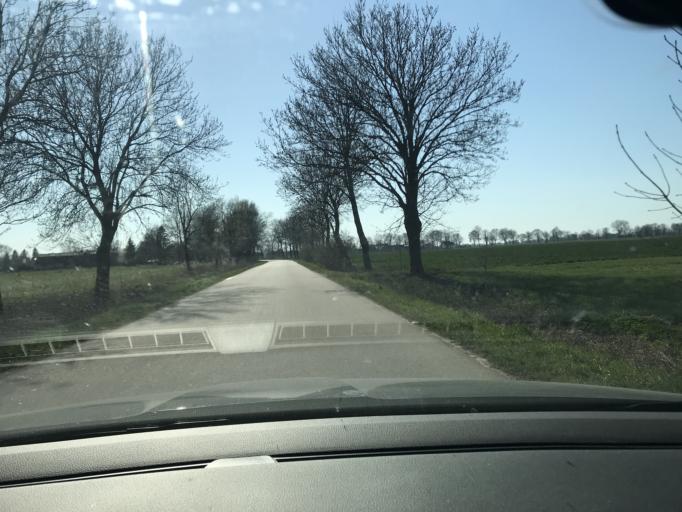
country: PL
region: Pomeranian Voivodeship
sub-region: Powiat nowodworski
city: Stegna
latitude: 54.2933
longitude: 19.1222
